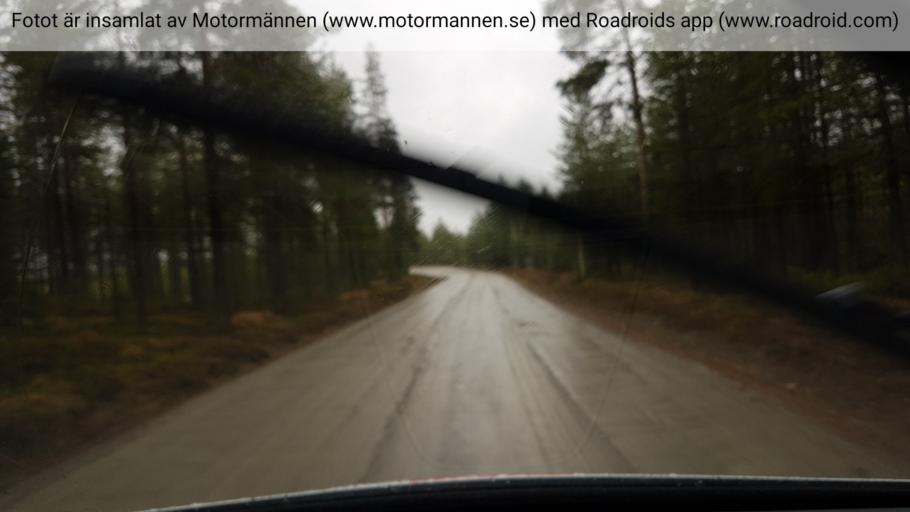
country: SE
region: Jaemtland
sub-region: Are Kommun
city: Jarpen
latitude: 62.4511
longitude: 13.5158
